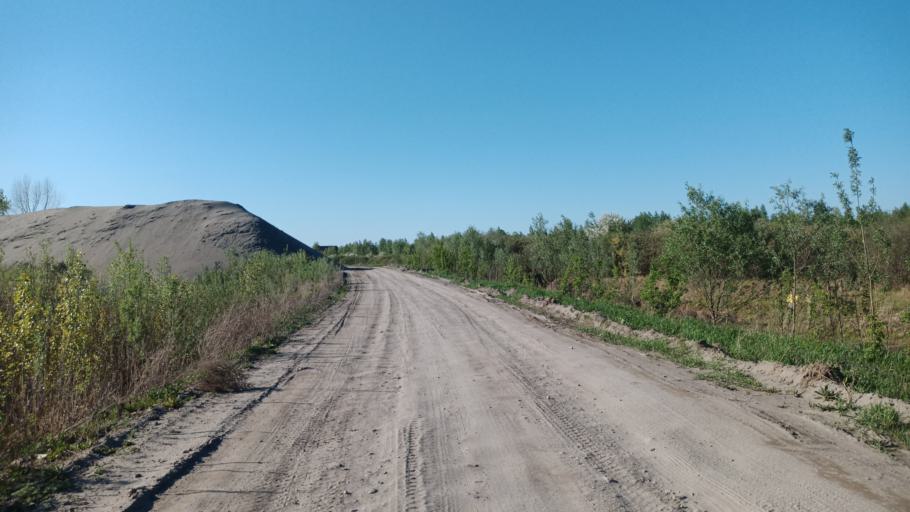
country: RU
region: Altai Krai
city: Zaton
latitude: 53.3086
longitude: 83.8236
